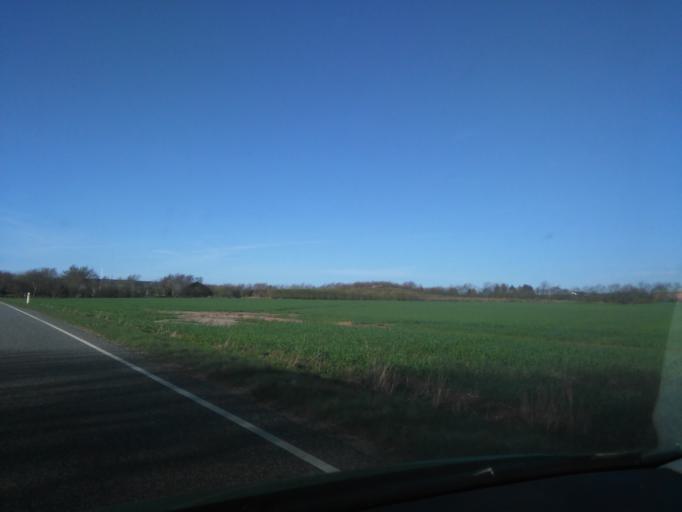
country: DK
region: Central Jutland
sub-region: Ringkobing-Skjern Kommune
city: Videbaek
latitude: 56.0747
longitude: 8.5070
